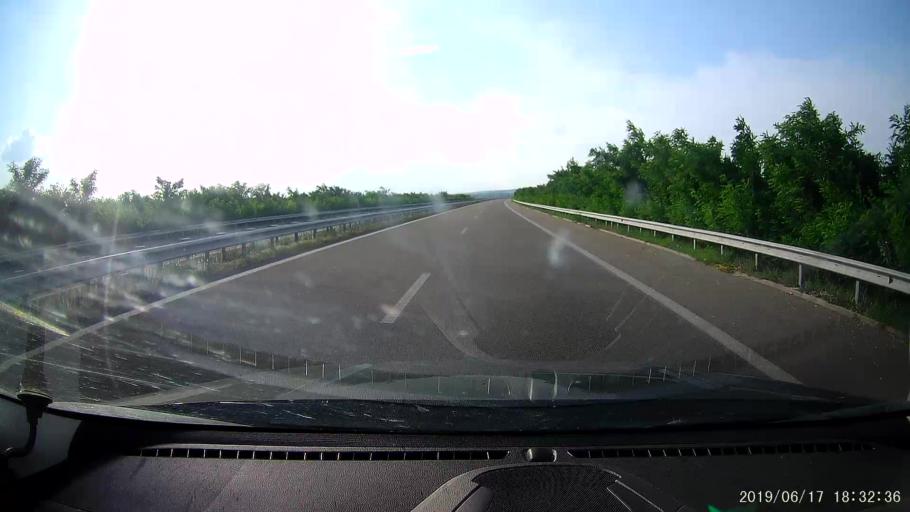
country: BG
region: Khaskovo
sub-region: Obshtina Dimitrovgrad
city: Dimitrovgrad
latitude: 42.0626
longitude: 25.4750
